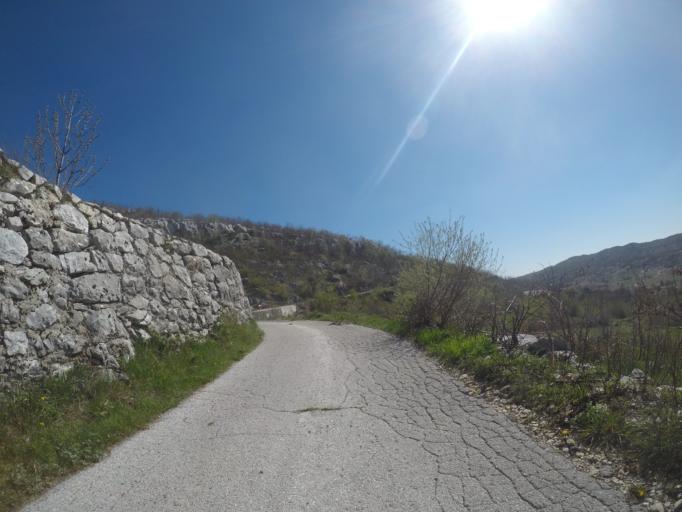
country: ME
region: Cetinje
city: Cetinje
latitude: 42.5281
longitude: 18.9496
